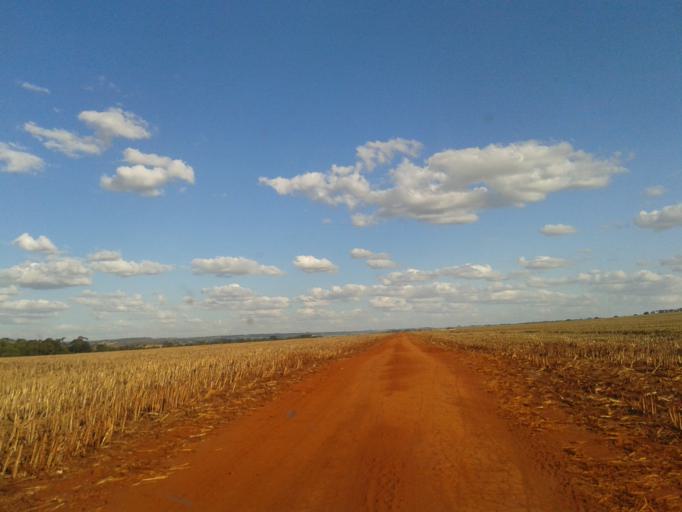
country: BR
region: Minas Gerais
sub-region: Centralina
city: Centralina
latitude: -18.5969
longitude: -49.2621
